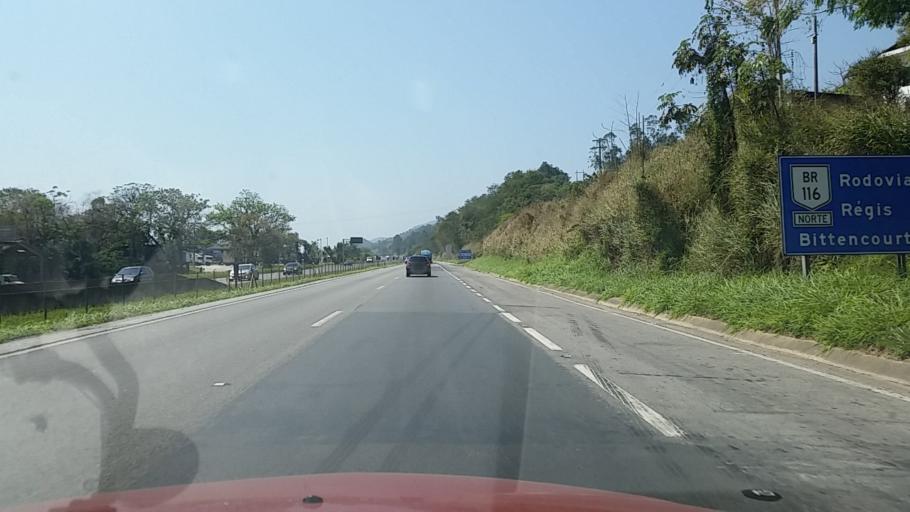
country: BR
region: Sao Paulo
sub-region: Miracatu
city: Miracatu
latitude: -24.2874
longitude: -47.4540
